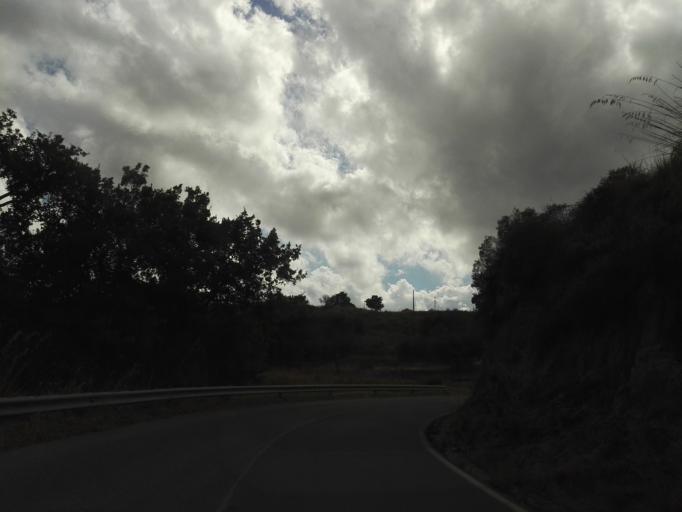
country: IT
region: Calabria
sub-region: Provincia di Reggio Calabria
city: Riace
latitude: 38.4239
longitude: 16.4838
